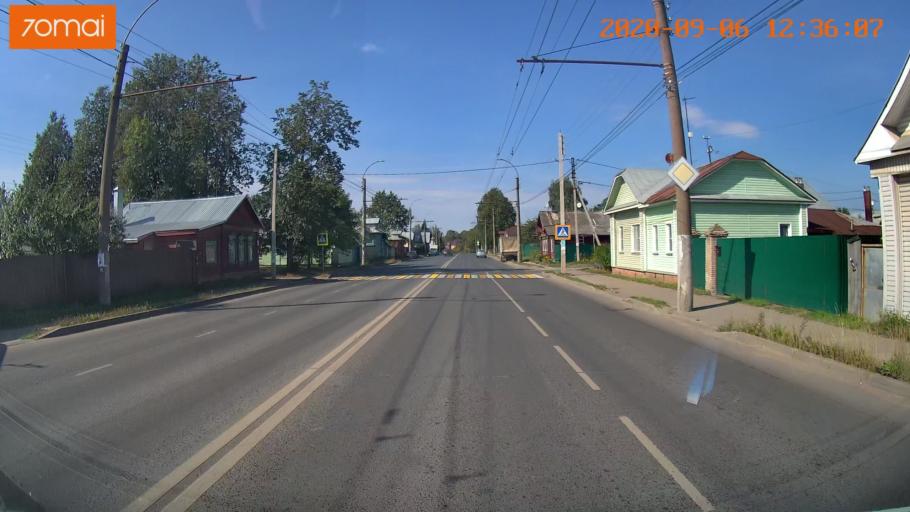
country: RU
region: Ivanovo
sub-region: Gorod Ivanovo
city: Ivanovo
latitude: 57.0217
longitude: 40.9880
